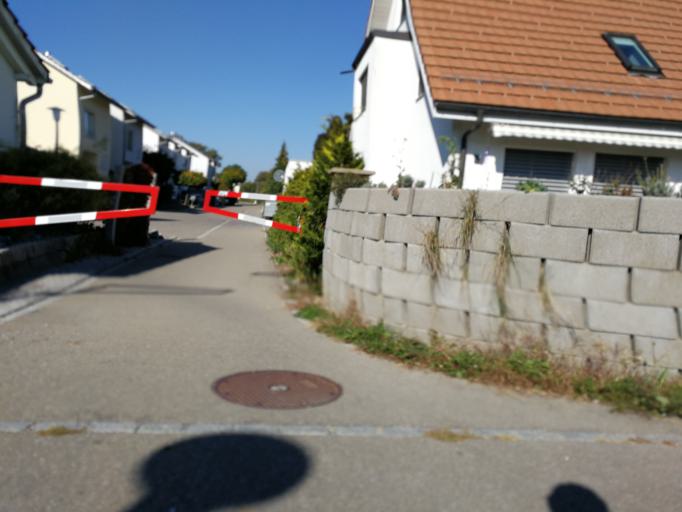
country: CH
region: Zurich
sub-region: Bezirk Uster
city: Moenchaltorf / Dorf
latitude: 47.3056
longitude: 8.7196
